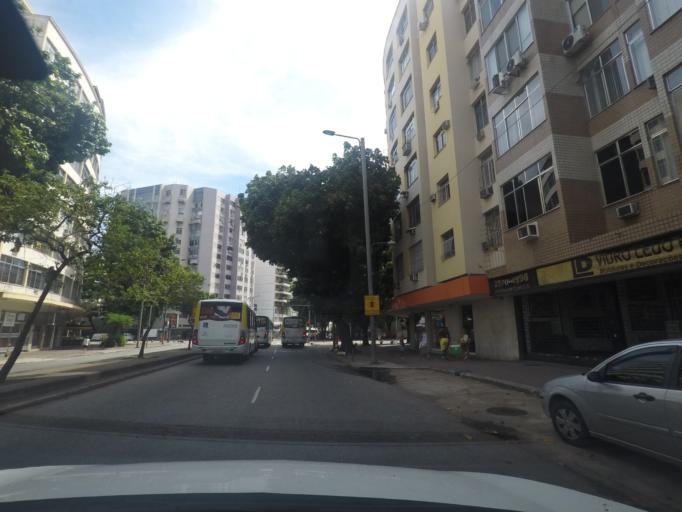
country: BR
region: Rio de Janeiro
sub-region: Rio De Janeiro
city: Rio de Janeiro
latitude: -22.9331
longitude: -43.2415
